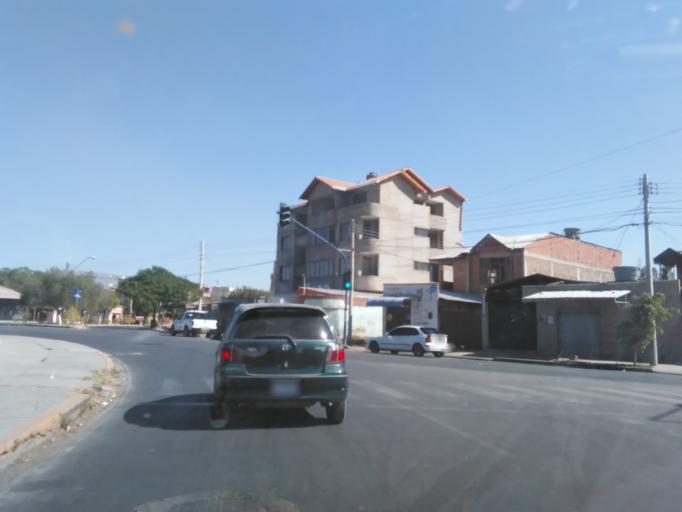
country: BO
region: Cochabamba
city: Cochabamba
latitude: -17.4148
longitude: -66.1628
